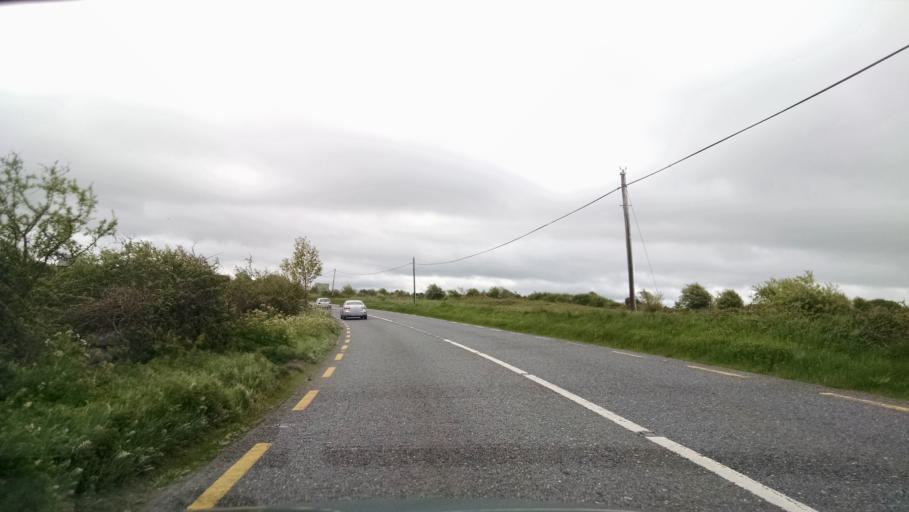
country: IE
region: Connaught
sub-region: County Galway
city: Oranmore
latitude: 53.1940
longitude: -8.8561
